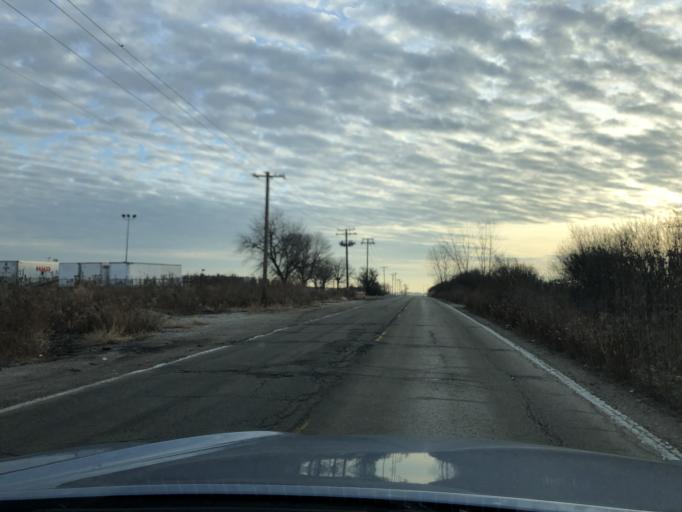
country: US
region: Illinois
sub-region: Cook County
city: Elk Grove Village
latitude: 42.0057
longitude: -87.9346
